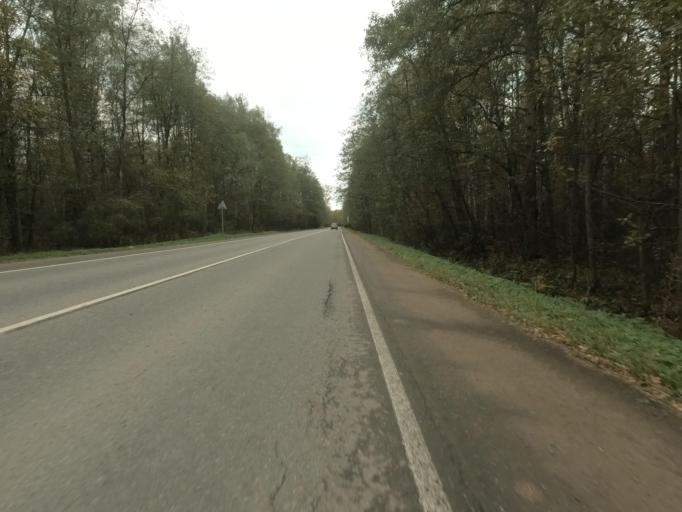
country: RU
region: Leningrad
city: Pavlovo
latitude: 59.7977
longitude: 30.9450
